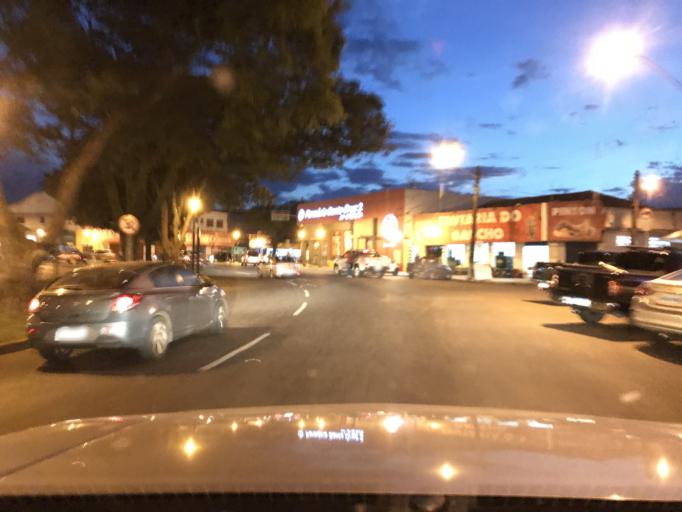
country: PY
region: Canindeyu
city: Salto del Guaira
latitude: -24.0830
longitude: -54.2445
